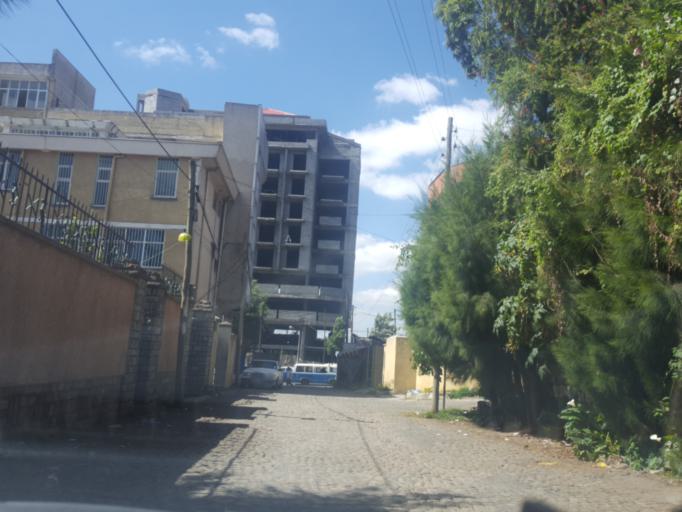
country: ET
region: Adis Abeba
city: Addis Ababa
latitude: 9.0556
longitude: 38.7421
